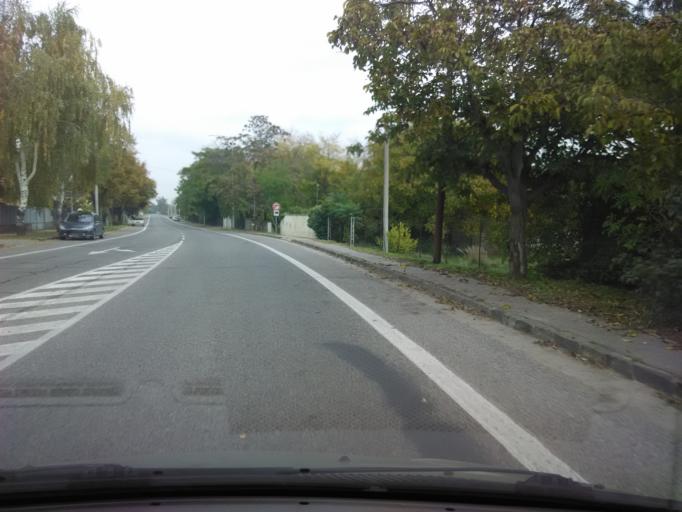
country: SK
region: Nitriansky
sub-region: Okres Komarno
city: Hurbanovo
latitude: 47.8907
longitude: 18.2017
